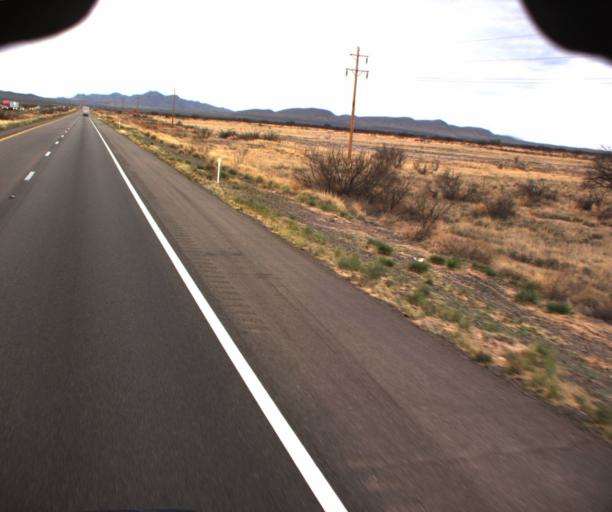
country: US
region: Arizona
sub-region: Cochise County
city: Willcox
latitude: 32.1939
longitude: -109.9206
